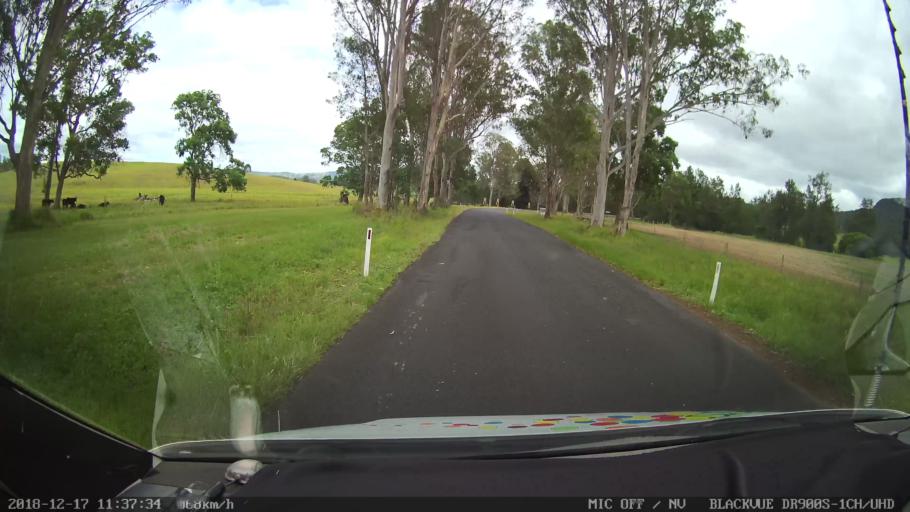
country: AU
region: New South Wales
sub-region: Kyogle
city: Kyogle
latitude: -28.7036
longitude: 152.6035
